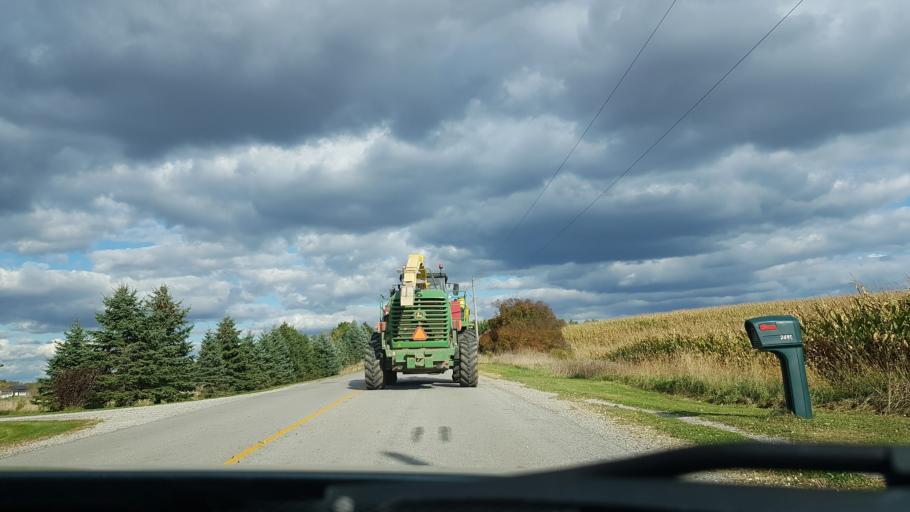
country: CA
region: Ontario
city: Delaware
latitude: 43.0120
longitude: -81.3784
